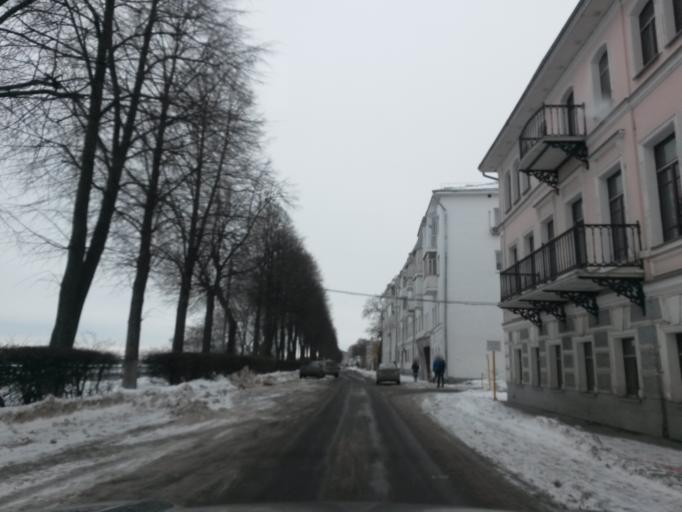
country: RU
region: Jaroslavl
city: Yaroslavl
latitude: 57.6379
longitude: 39.8894
